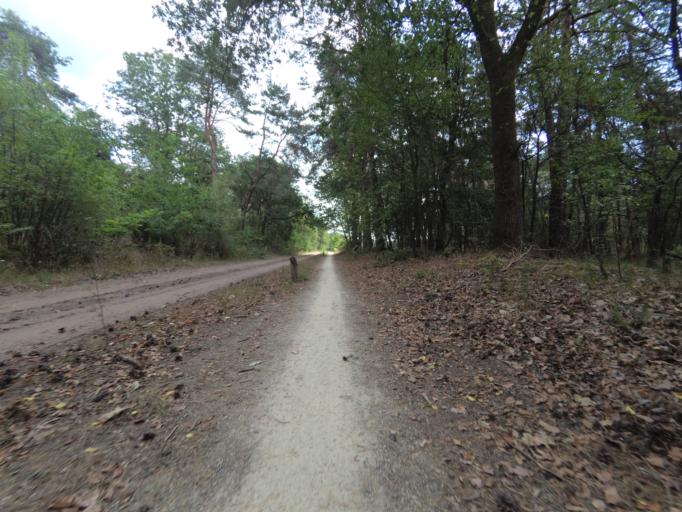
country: NL
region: Overijssel
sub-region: Gemeente Haaksbergen
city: Haaksbergen
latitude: 52.1267
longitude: 6.7396
